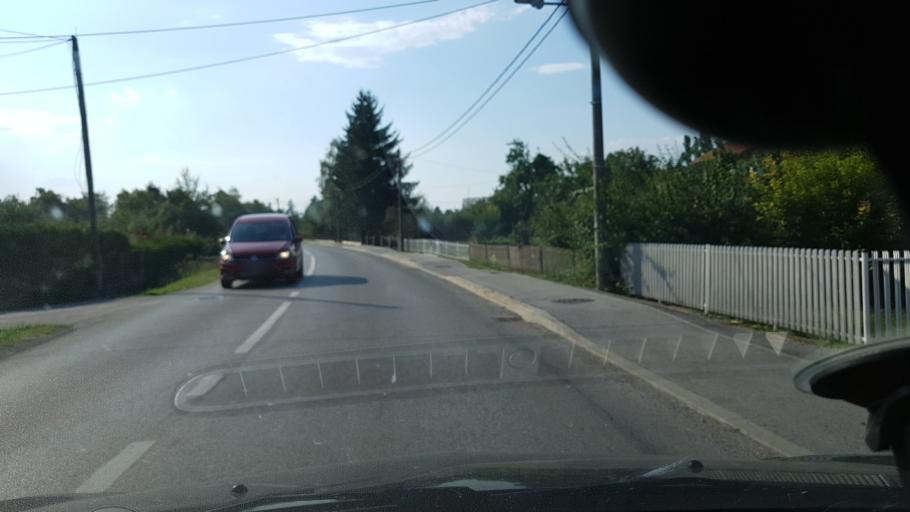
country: HR
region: Zagrebacka
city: Bregana
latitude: 45.8865
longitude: 15.7001
